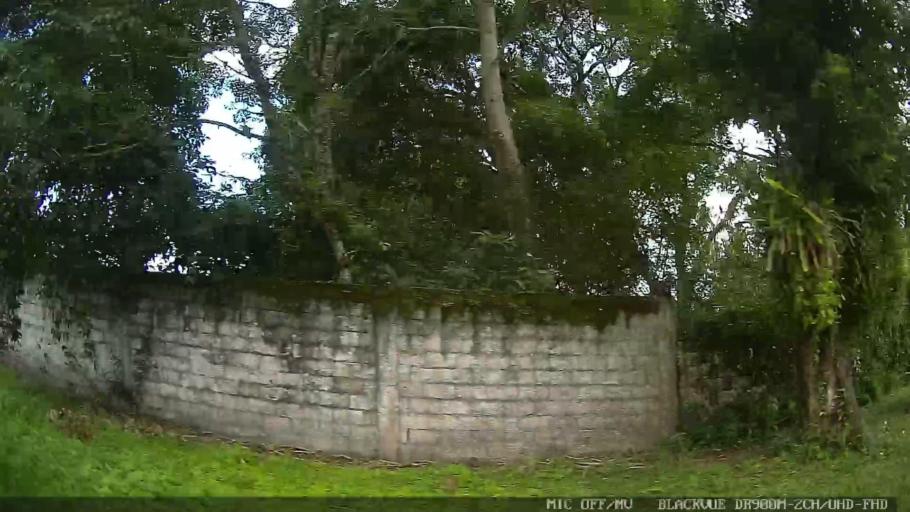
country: BR
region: Sao Paulo
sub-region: Iguape
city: Iguape
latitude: -24.6930
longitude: -47.5306
